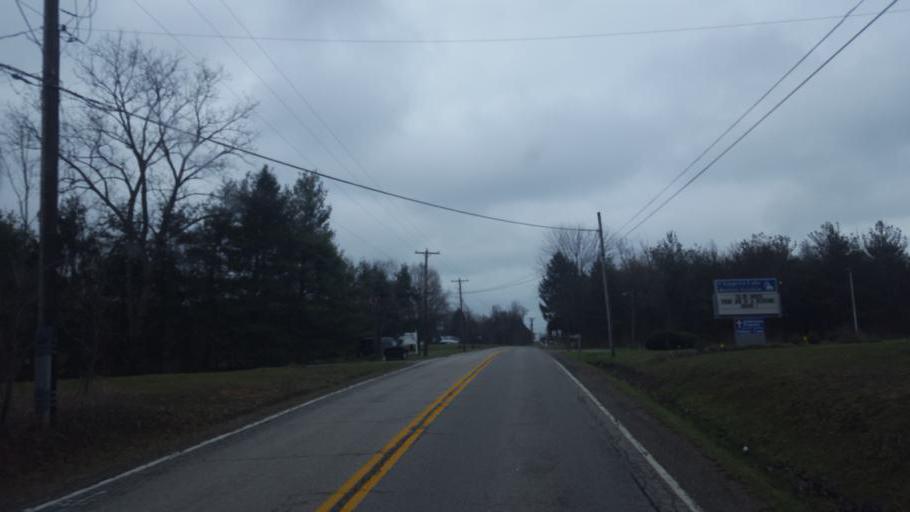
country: US
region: Ohio
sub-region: Medina County
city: Medina
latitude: 41.0768
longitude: -81.8815
